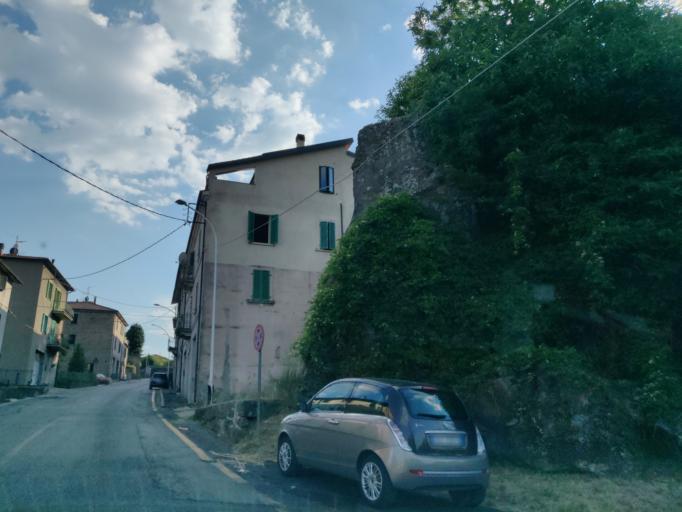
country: IT
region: Tuscany
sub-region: Provincia di Siena
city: Piancastagnaio
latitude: 42.8513
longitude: 11.6938
